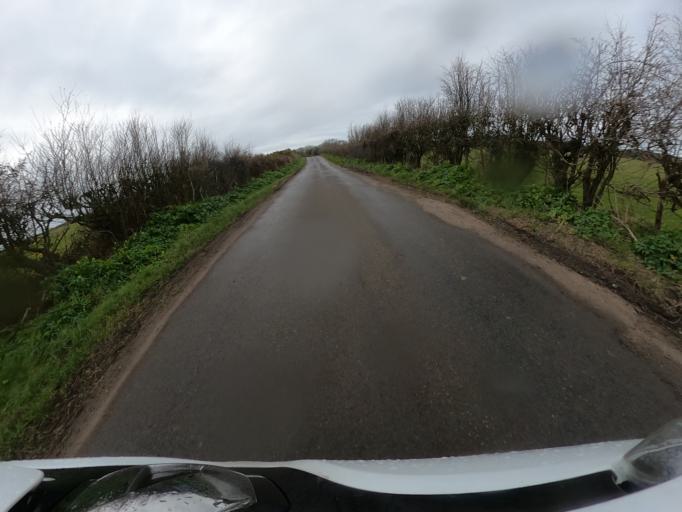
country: IM
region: Ramsey
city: Ramsey
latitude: 54.3812
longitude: -4.4624
